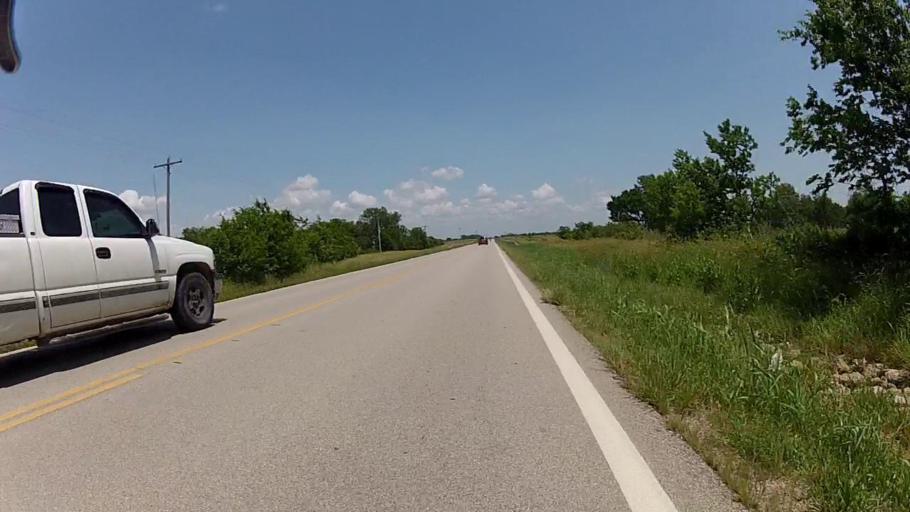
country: US
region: Kansas
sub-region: Montgomery County
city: Cherryvale
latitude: 37.1928
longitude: -95.4662
